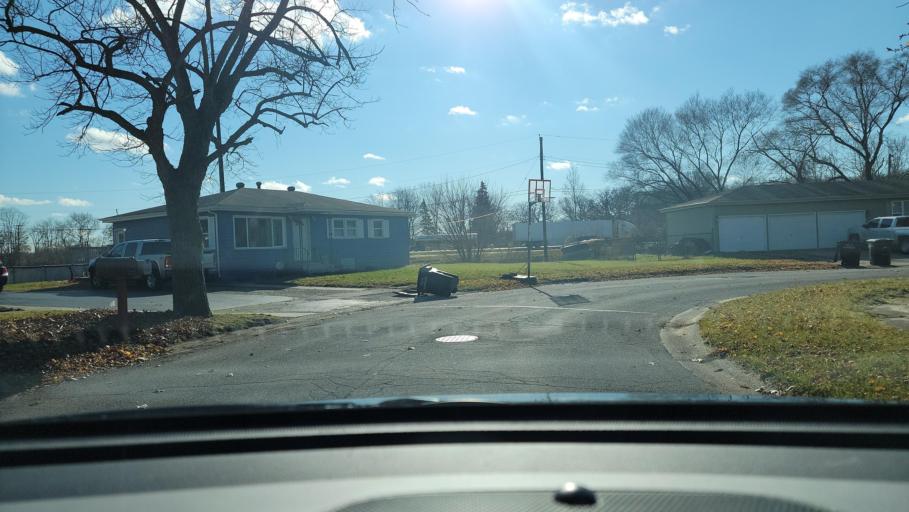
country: US
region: Indiana
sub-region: Porter County
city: Portage
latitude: 41.5815
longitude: -87.1856
